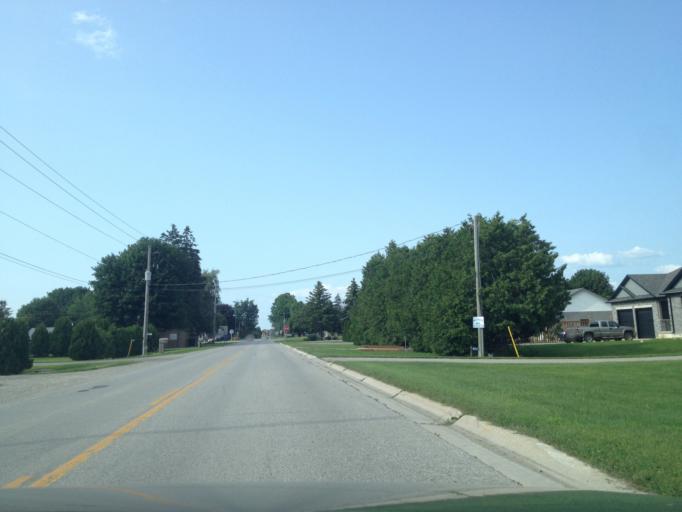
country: CA
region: Ontario
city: Aylmer
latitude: 42.7091
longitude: -80.8591
